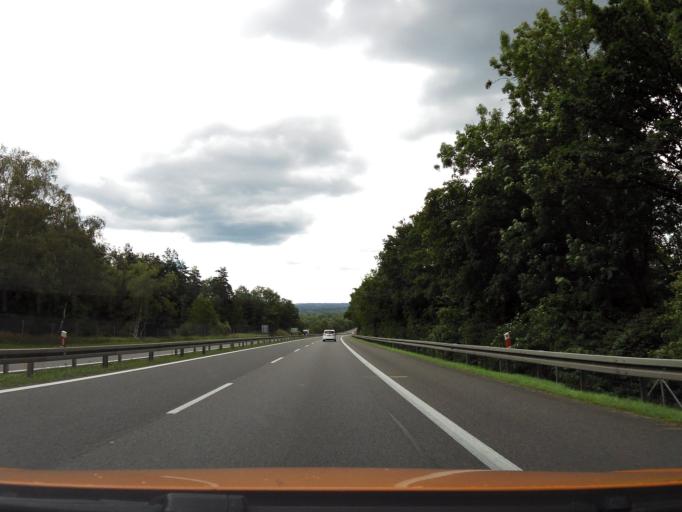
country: PL
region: West Pomeranian Voivodeship
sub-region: Powiat policki
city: Przeclaw
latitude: 53.3415
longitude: 14.4820
